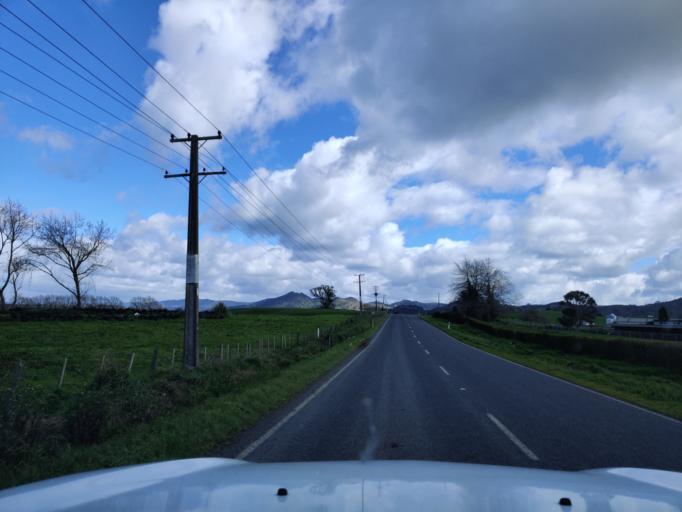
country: NZ
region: Waikato
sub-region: Waikato District
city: Ngaruawahia
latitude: -37.5730
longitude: 175.2466
